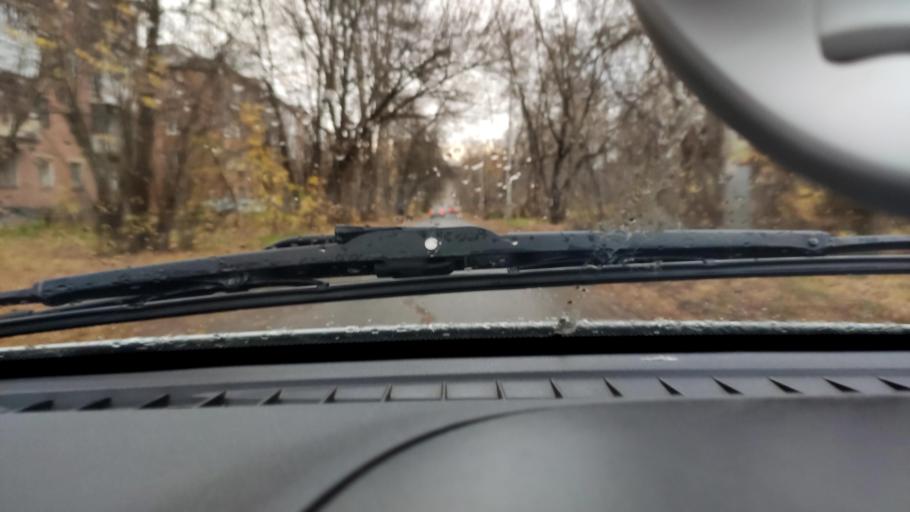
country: RU
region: Perm
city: Perm
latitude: 57.9605
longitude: 56.2393
